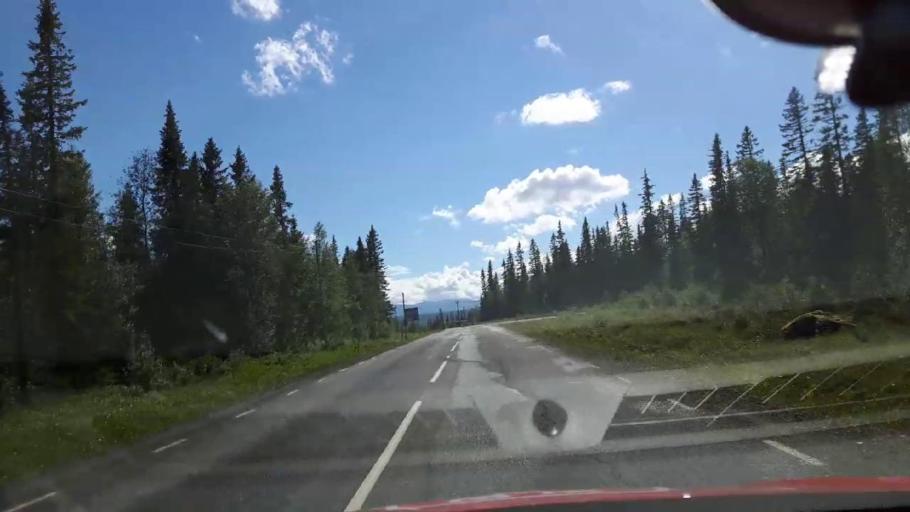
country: SE
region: Jaemtland
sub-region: Are Kommun
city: Are
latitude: 63.2300
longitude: 13.1608
